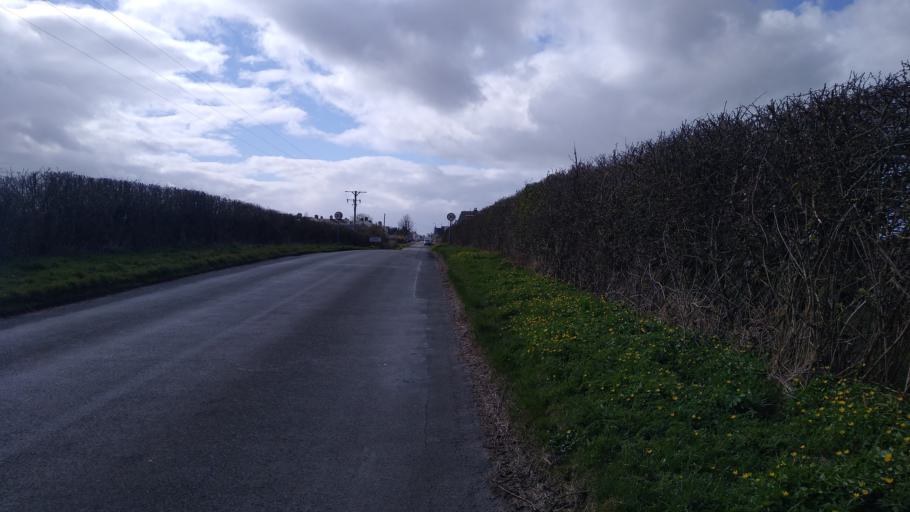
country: GB
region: England
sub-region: Cumbria
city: Dearham
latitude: 54.6888
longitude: -3.4622
